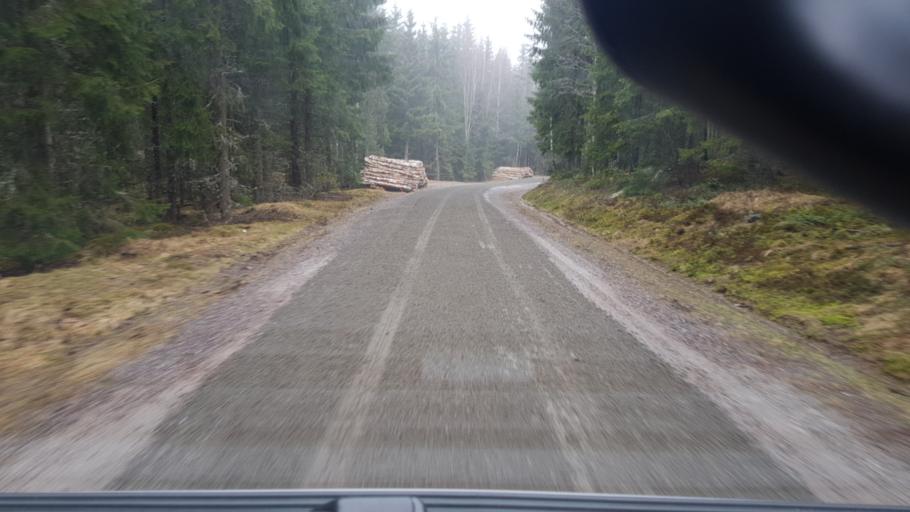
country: SE
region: Vaermland
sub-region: Eda Kommun
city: Amotfors
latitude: 59.8529
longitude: 12.5098
